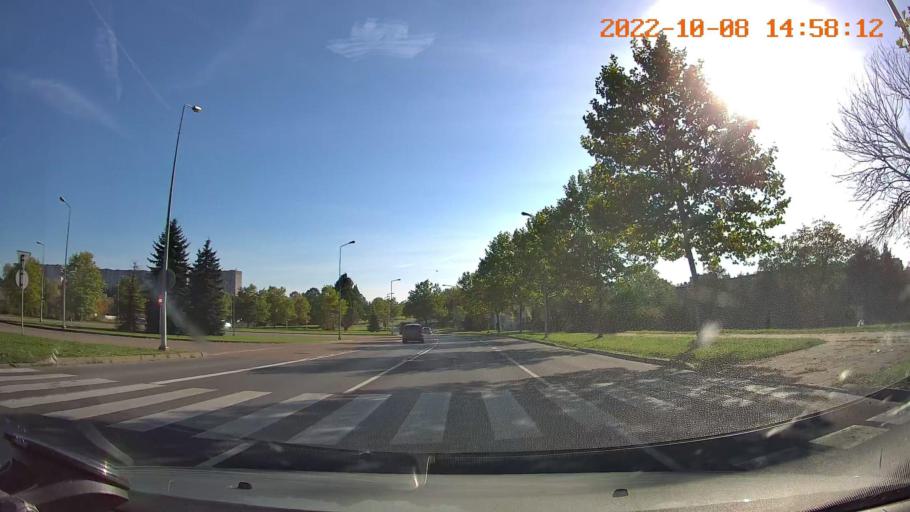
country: PL
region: Lesser Poland Voivodeship
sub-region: Powiat tarnowski
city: Tarnow
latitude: 50.0253
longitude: 20.9979
